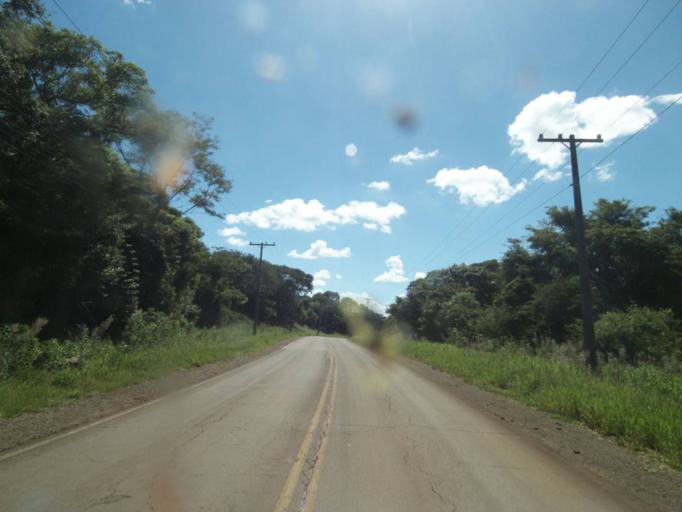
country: BR
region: Parana
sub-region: Chopinzinho
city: Chopinzinho
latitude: -25.7864
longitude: -52.0975
